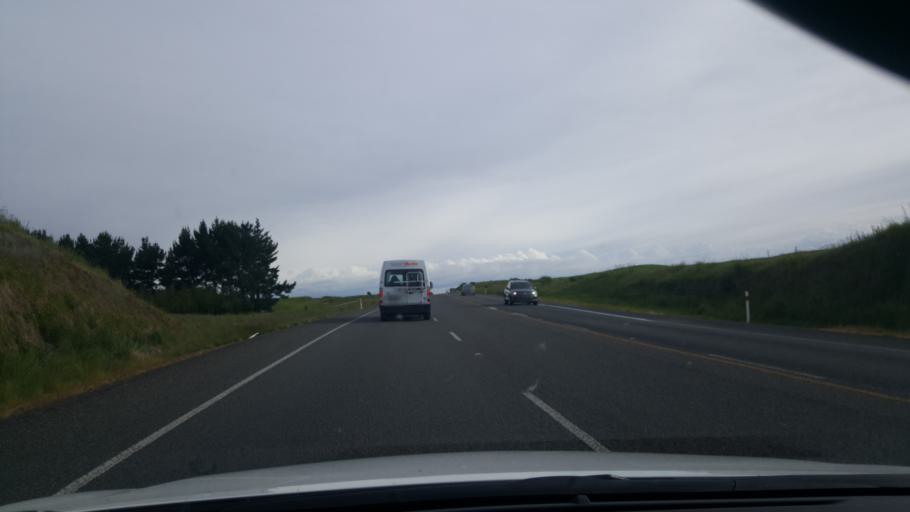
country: NZ
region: Waikato
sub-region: Taupo District
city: Taupo
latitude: -38.6422
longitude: 176.0995
